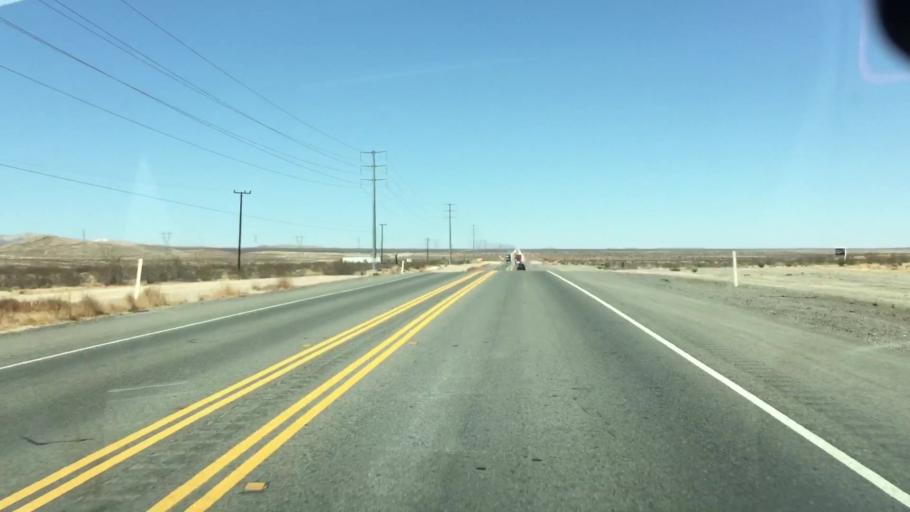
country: US
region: California
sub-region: San Bernardino County
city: Adelanto
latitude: 34.6468
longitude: -117.4352
